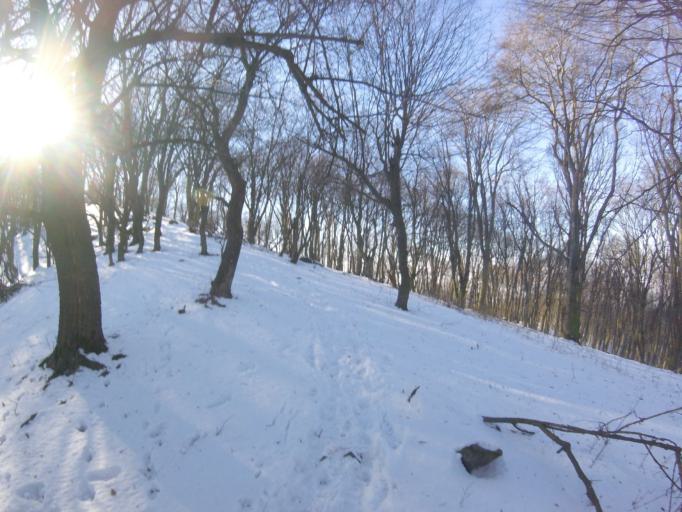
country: SK
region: Nitriansky
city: Sahy
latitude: 47.9689
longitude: 18.8810
